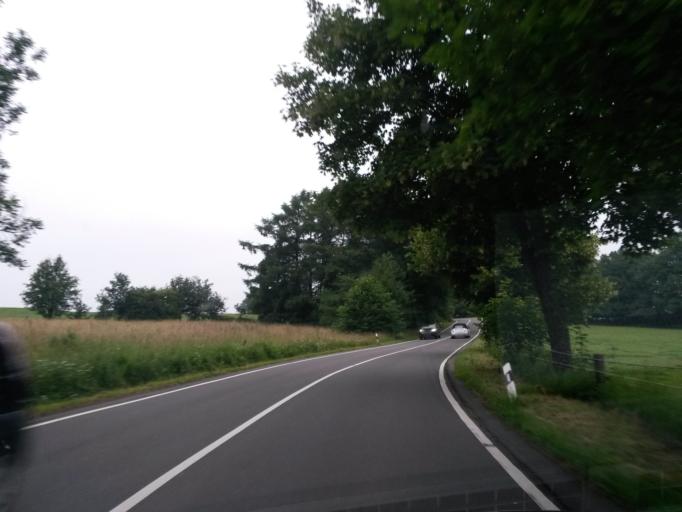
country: DE
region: North Rhine-Westphalia
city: Meinerzhagen
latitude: 51.1108
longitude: 7.6249
